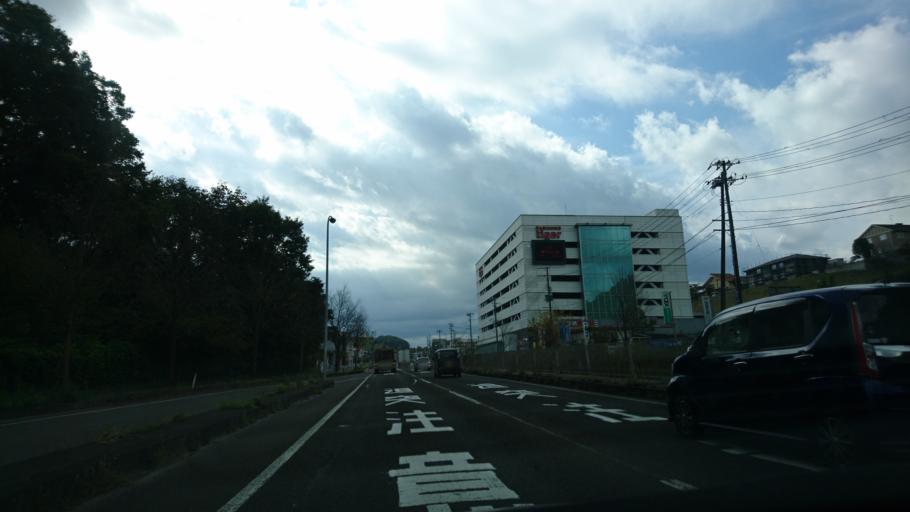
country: JP
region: Miyagi
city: Tomiya
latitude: 38.3721
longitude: 140.8741
